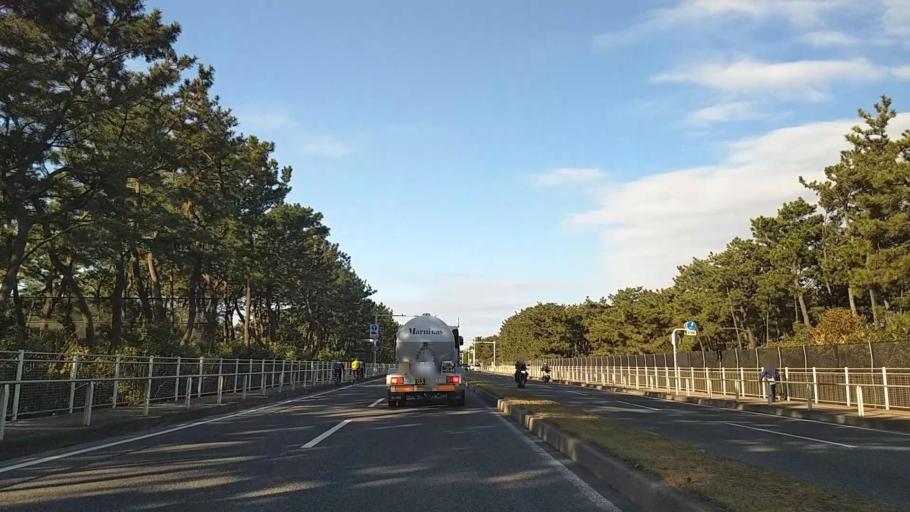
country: JP
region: Kanagawa
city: Chigasaki
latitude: 35.3184
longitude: 139.4108
